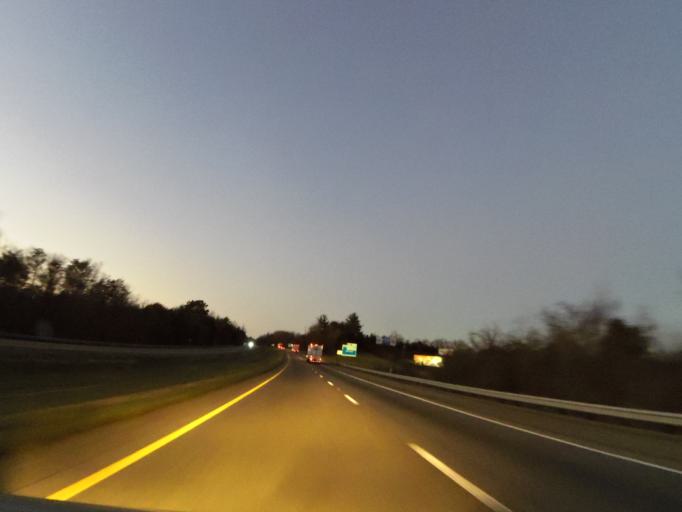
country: US
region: Tennessee
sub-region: Cocke County
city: Newport
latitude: 35.9217
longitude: -83.1886
